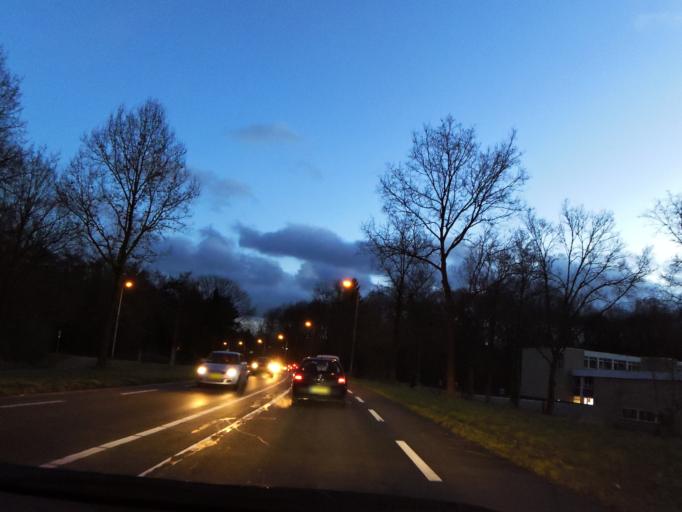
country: NL
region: Limburg
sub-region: Gemeente Roerdalen
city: Melick
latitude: 51.1716
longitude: 6.0023
